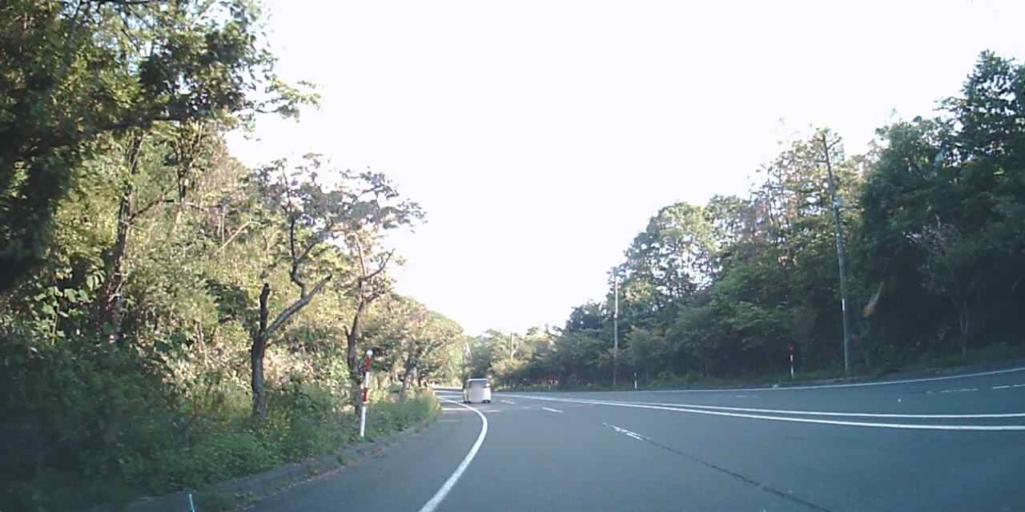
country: JP
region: Hokkaido
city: Shiraoi
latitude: 42.4622
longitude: 141.1772
